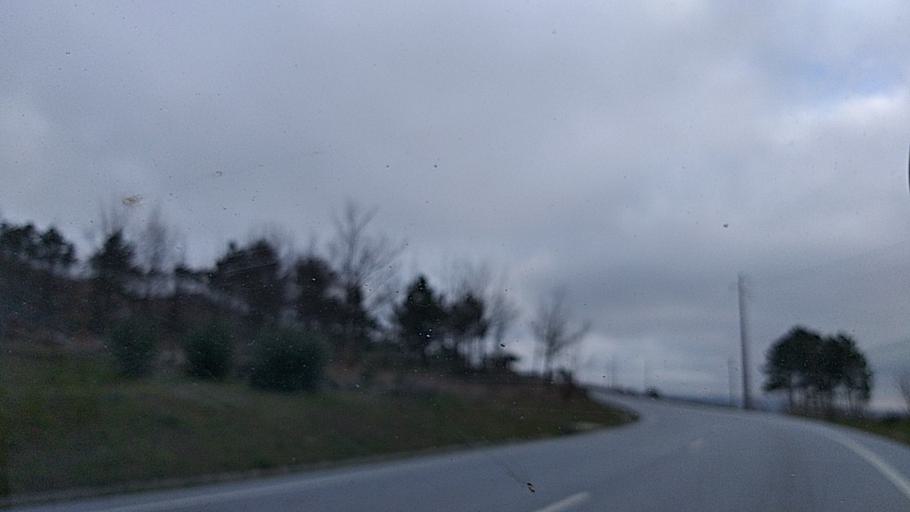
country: PT
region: Guarda
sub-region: Fornos de Algodres
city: Fornos de Algodres
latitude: 40.6597
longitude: -7.4797
